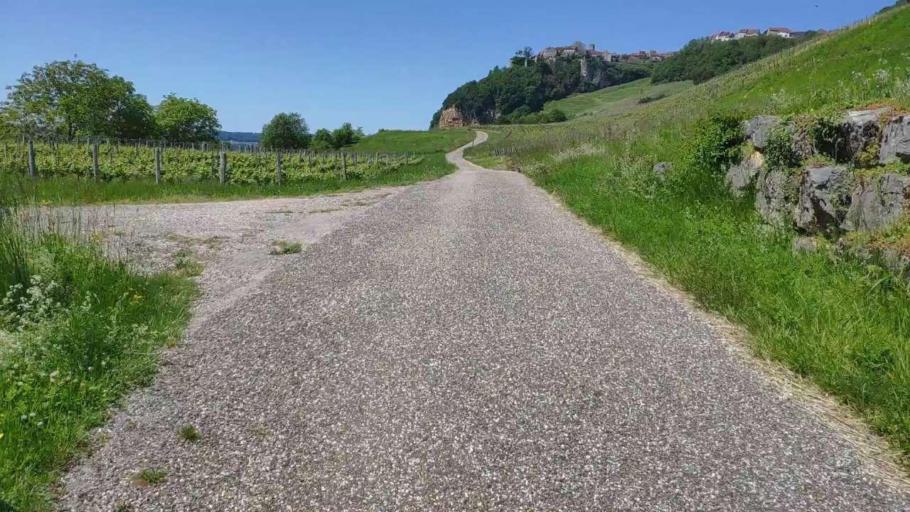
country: FR
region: Franche-Comte
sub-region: Departement du Jura
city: Perrigny
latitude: 46.7456
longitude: 5.6288
